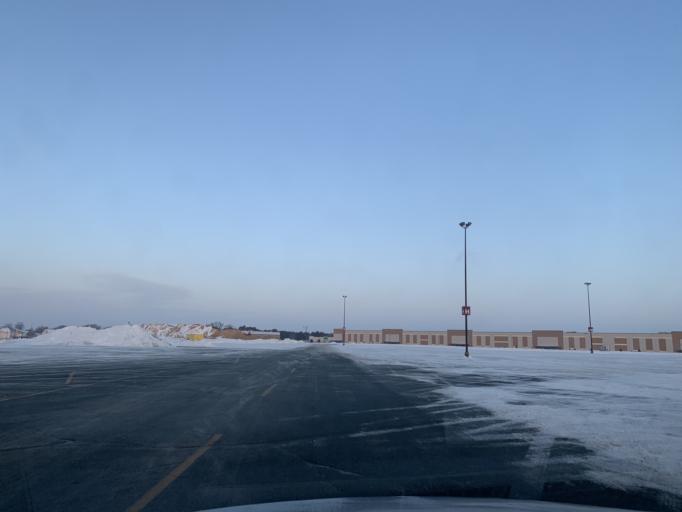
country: US
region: Minnesota
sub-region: Scott County
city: Shakopee
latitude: 44.7918
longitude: -93.4849
